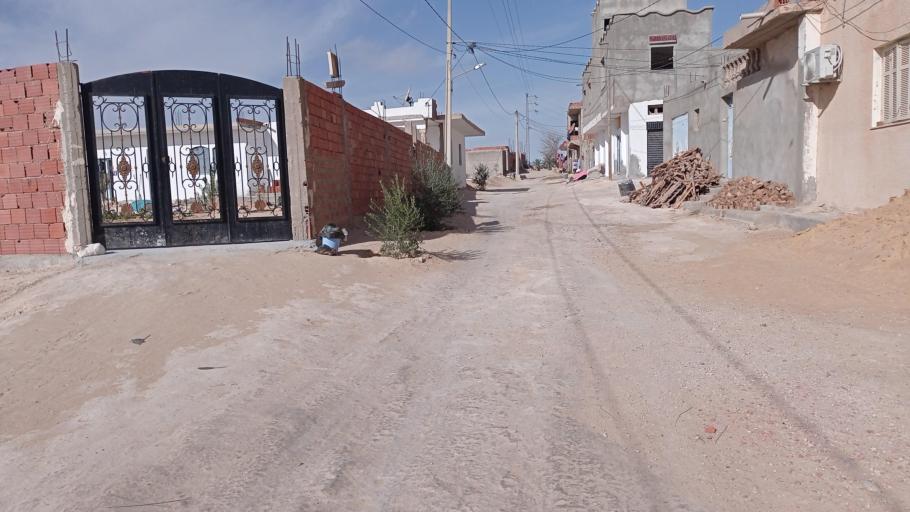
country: TN
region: Qabis
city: Gabes
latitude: 33.8338
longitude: 10.1101
